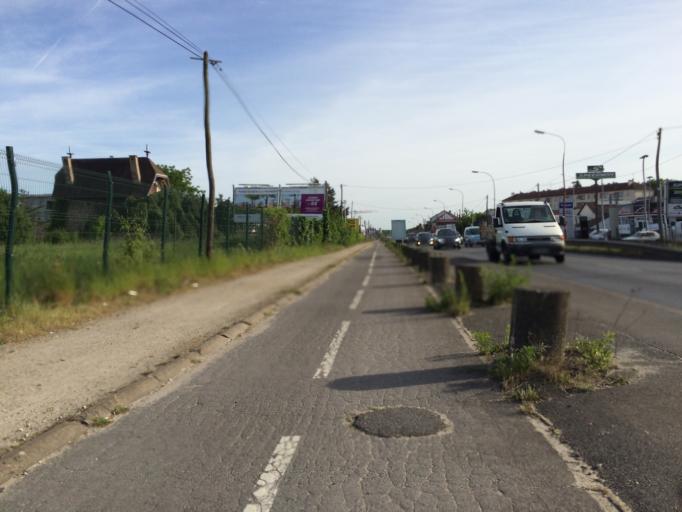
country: FR
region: Ile-de-France
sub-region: Departement de l'Essonne
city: Montlhery
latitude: 48.6468
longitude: 2.2710
